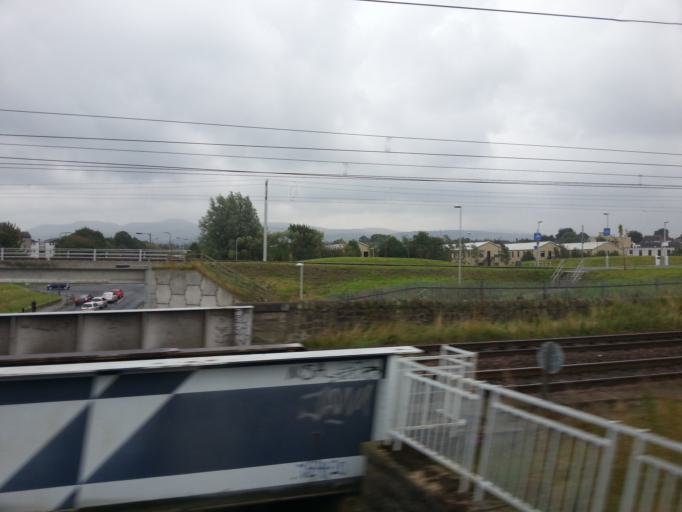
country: GB
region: Scotland
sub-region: Edinburgh
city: Colinton
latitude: 55.9328
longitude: -3.2747
